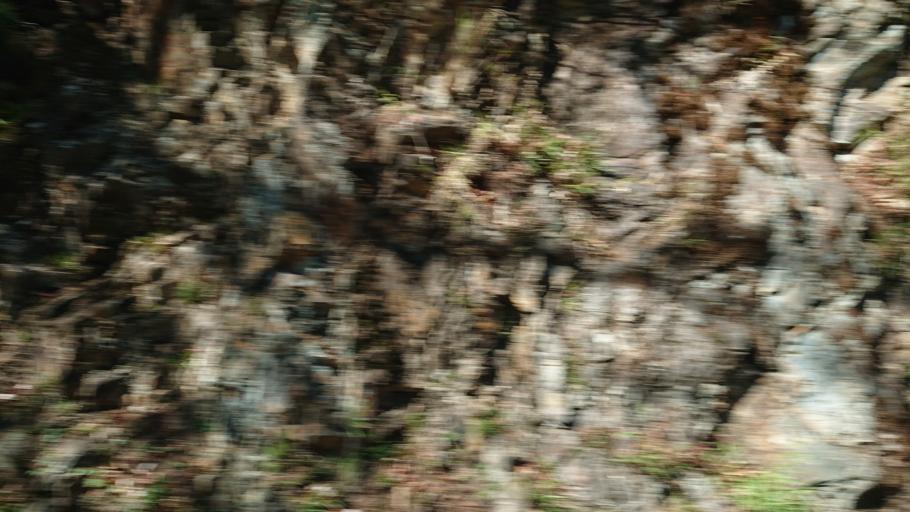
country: TW
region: Taiwan
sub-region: Hualien
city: Hualian
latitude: 24.3439
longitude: 121.3104
